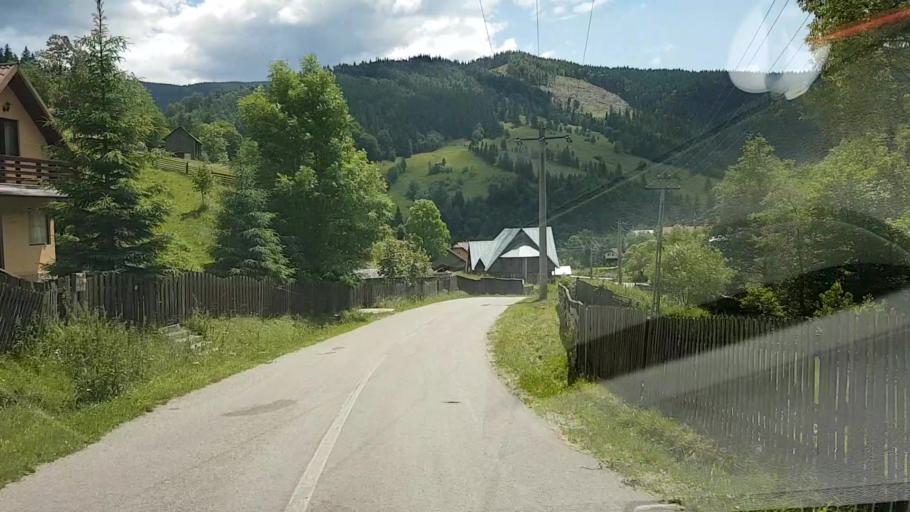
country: RO
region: Suceava
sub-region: Comuna Crucea
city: Crucea
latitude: 47.4201
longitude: 25.5802
